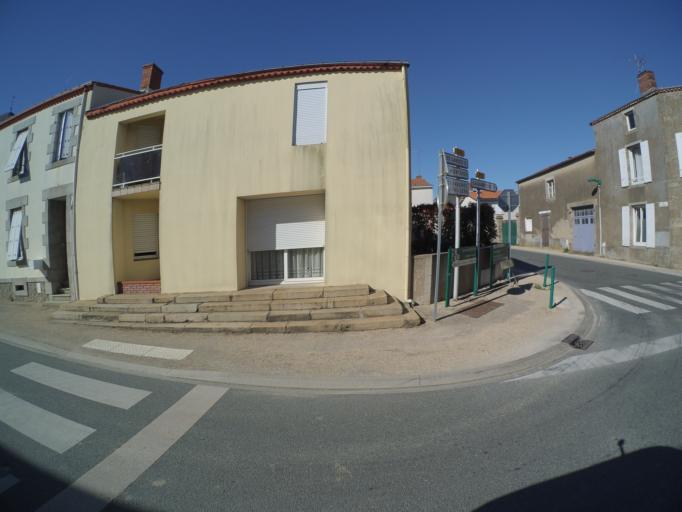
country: FR
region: Pays de la Loire
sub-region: Departement de la Vendee
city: Beaurepaire
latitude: 46.9073
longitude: -1.1329
